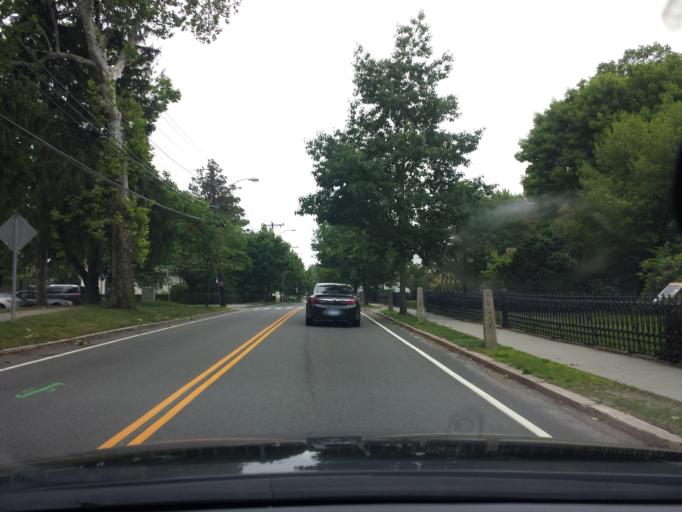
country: US
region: Connecticut
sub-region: New London County
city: Mystic
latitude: 41.3621
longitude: -71.9634
